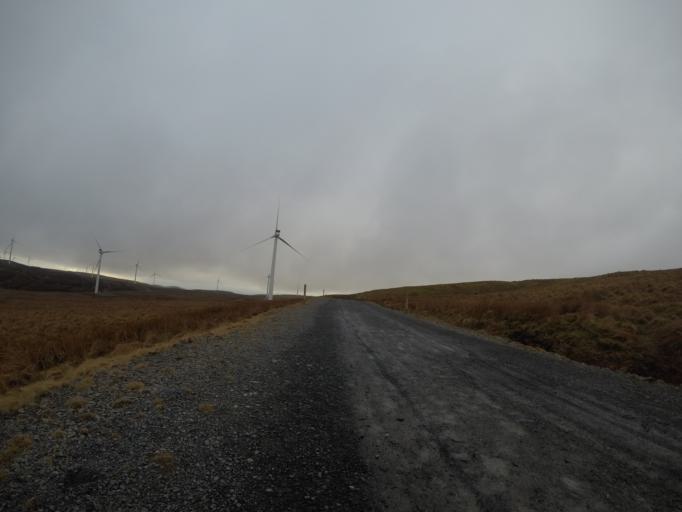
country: GB
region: Scotland
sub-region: North Ayrshire
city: Fairlie
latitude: 55.7596
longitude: -4.7927
